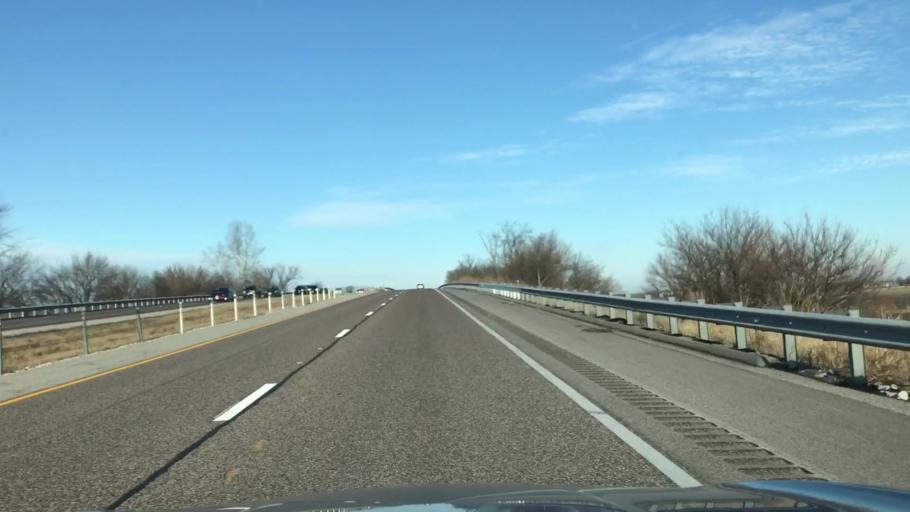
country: US
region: Illinois
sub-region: Madison County
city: Edwardsville
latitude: 38.8229
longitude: -89.8844
